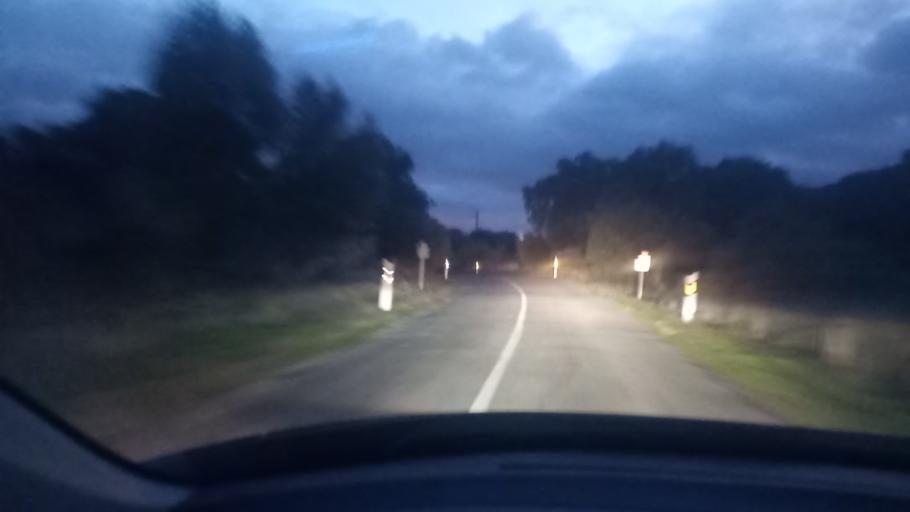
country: ES
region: Madrid
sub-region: Provincia de Madrid
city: Colmenar del Arroyo
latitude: 40.4337
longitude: -4.2240
